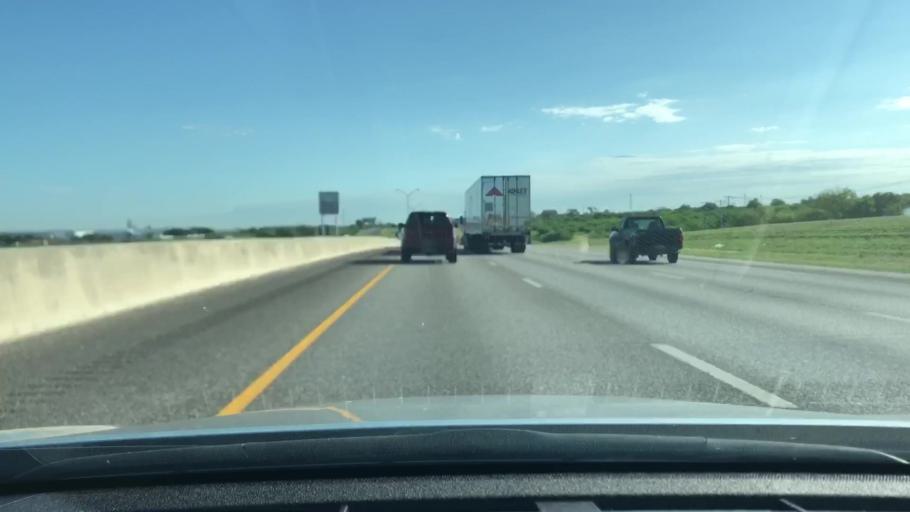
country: US
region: Texas
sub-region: Guadalupe County
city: Northcliff
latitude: 29.6334
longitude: -98.2239
